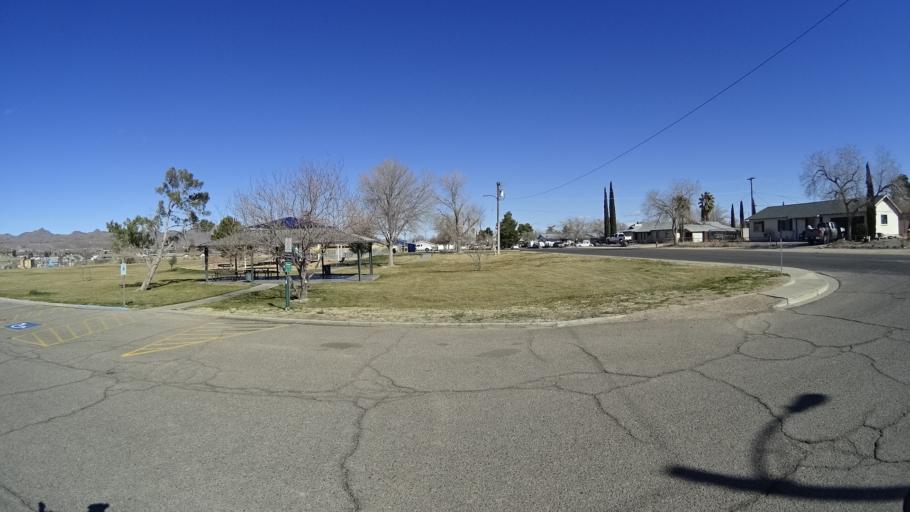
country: US
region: Arizona
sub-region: Mohave County
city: Kingman
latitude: 35.1940
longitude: -114.0227
